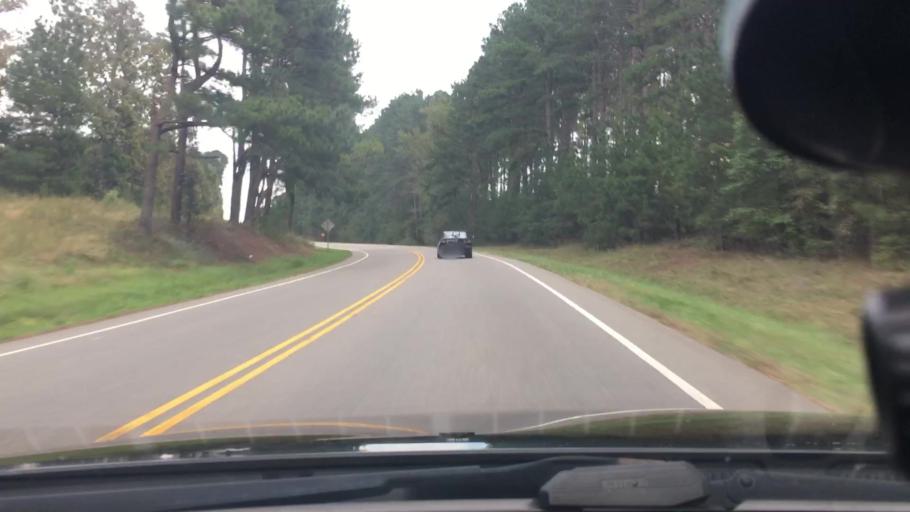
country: US
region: North Carolina
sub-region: Moore County
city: Carthage
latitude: 35.3785
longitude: -79.4738
